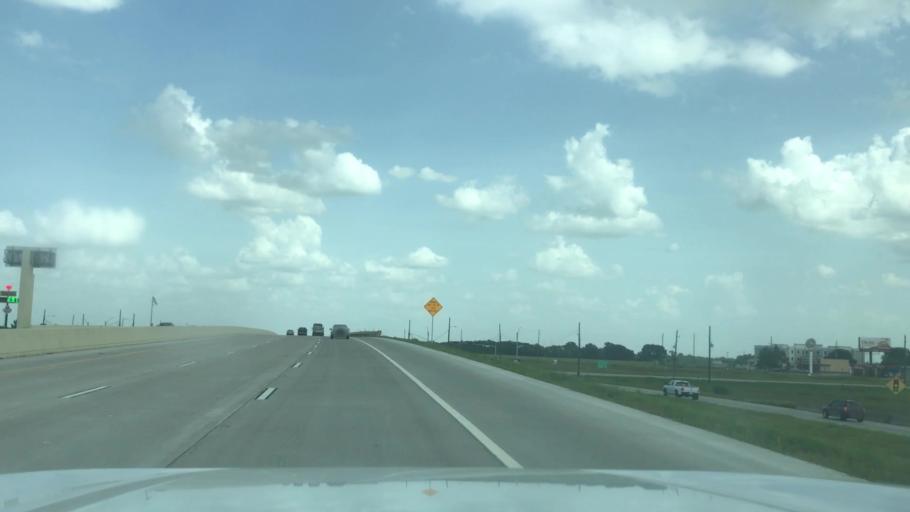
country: US
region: Texas
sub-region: Waller County
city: Waller
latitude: 30.0641
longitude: -95.9115
